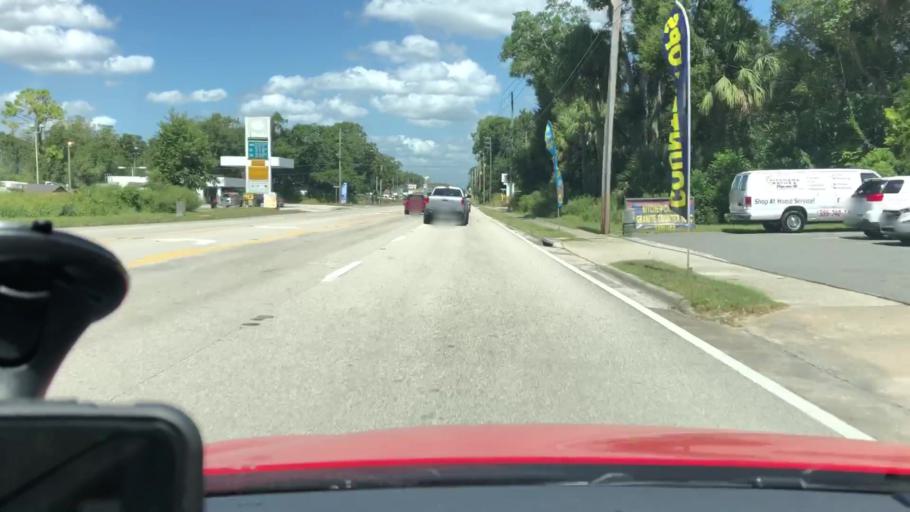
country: US
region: Florida
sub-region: Volusia County
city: West DeLand
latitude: 29.0158
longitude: -81.3238
